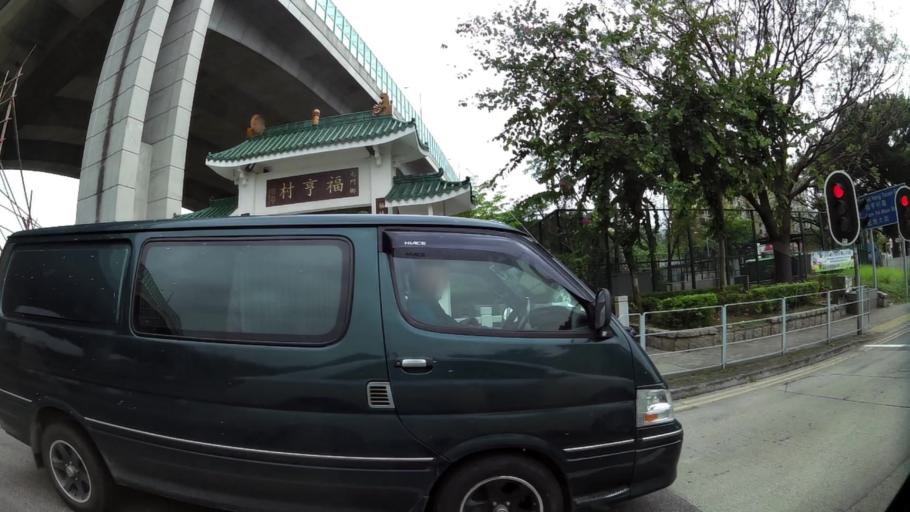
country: HK
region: Tuen Mun
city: Tuen Mun
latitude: 22.4217
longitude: 113.9849
